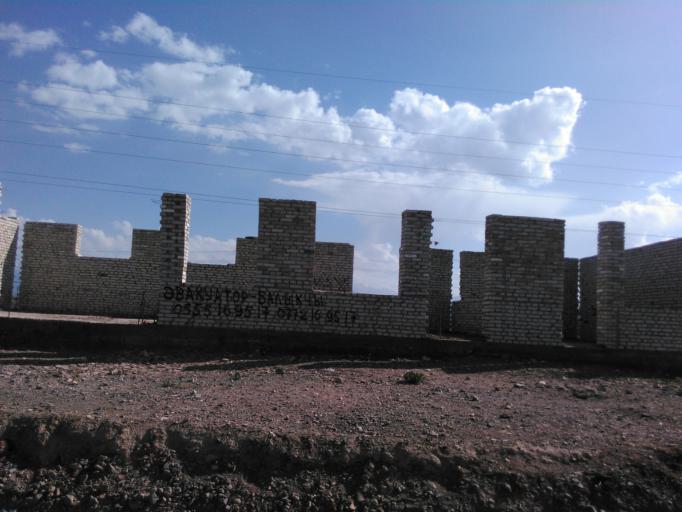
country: KG
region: Ysyk-Koel
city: Balykchy
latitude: 42.4539
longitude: 76.1583
